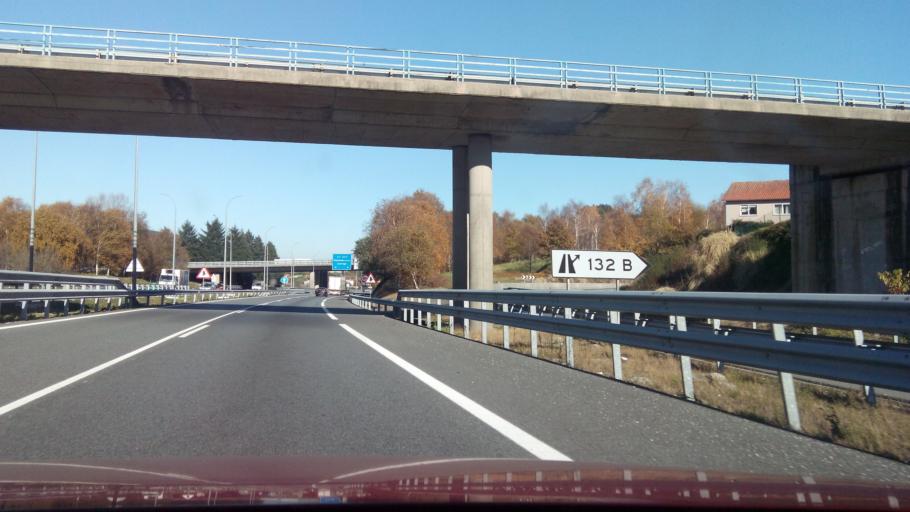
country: ES
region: Galicia
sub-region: Provincia de Pontevedra
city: Poio
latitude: 42.4116
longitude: -8.6539
